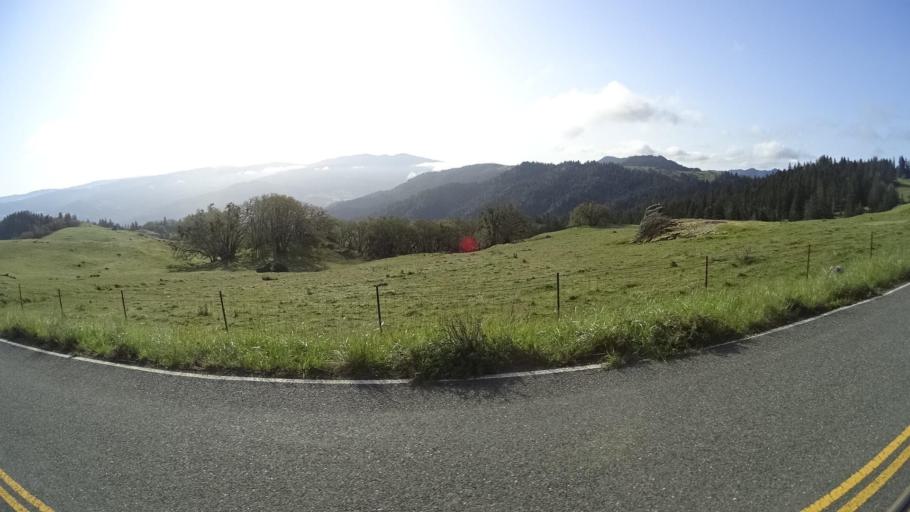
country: US
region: California
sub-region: Humboldt County
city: Blue Lake
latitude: 40.7358
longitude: -123.9460
